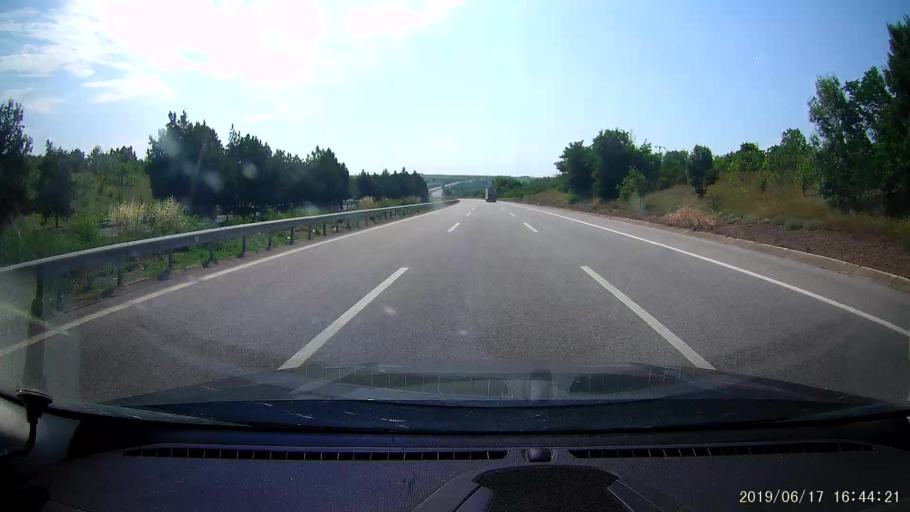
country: TR
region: Kirklareli
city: Luleburgaz
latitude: 41.4810
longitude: 27.2641
